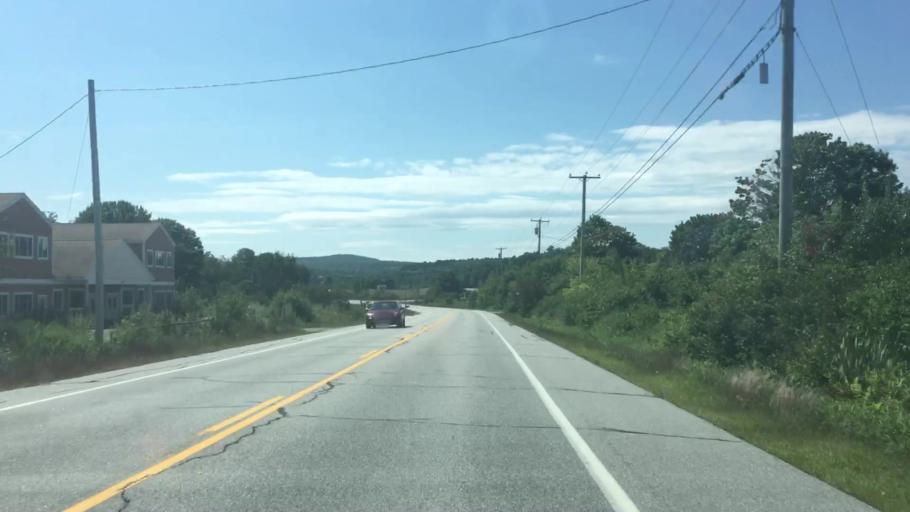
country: US
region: Maine
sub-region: Kennebec County
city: Monmouth
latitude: 44.1662
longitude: -70.0247
